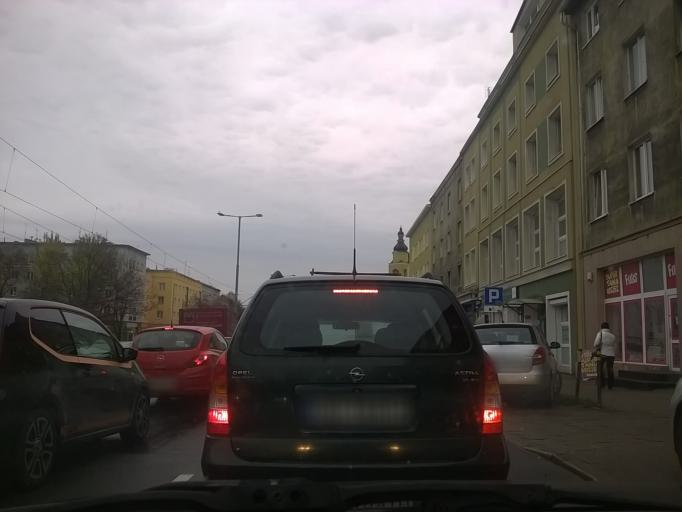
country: PL
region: Pomeranian Voivodeship
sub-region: Gdansk
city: Gdansk
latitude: 54.3771
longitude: 18.6099
